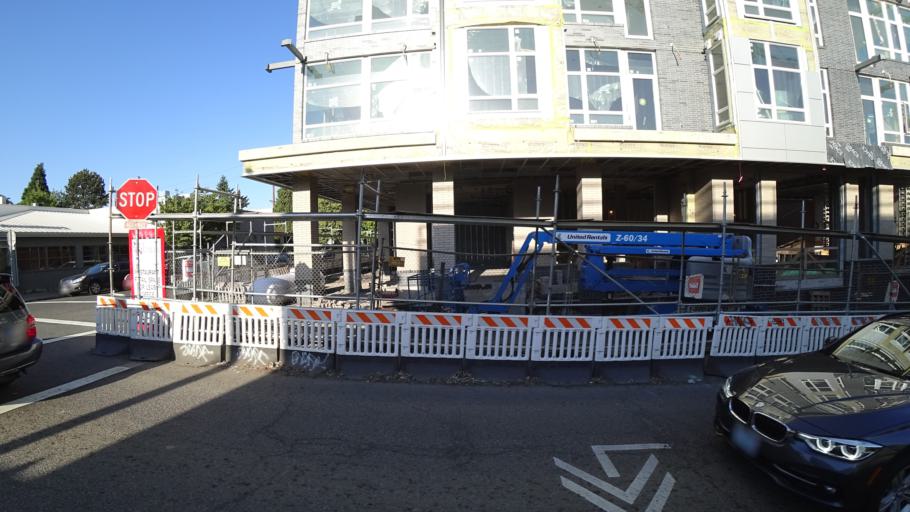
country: US
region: Oregon
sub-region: Multnomah County
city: Portland
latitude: 45.5477
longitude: -122.6756
